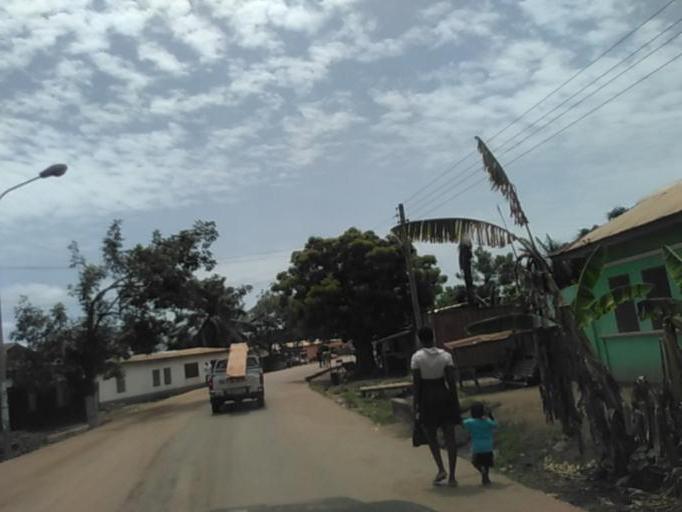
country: GH
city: Akropong
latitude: 6.1002
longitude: 0.1268
